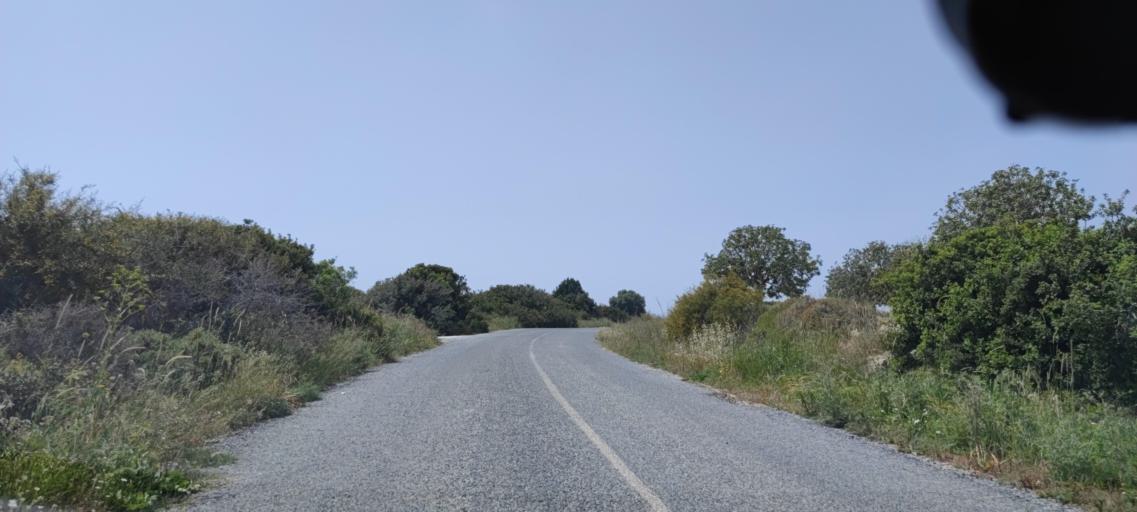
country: CY
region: Ammochostos
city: Rizokarpaso
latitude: 35.5221
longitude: 34.3198
